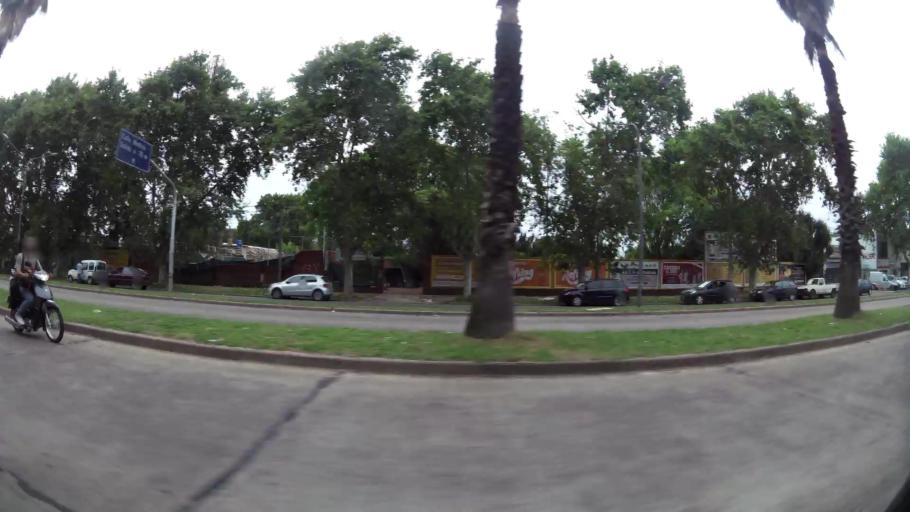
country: AR
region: Santa Fe
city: Granadero Baigorria
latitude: -32.8865
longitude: -60.6949
